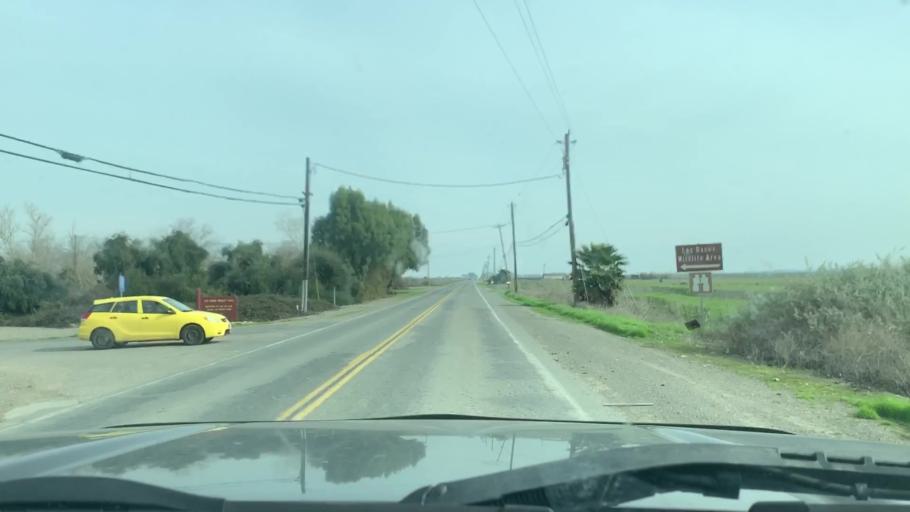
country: US
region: California
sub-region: Merced County
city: Los Banos
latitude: 37.0996
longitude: -120.8207
